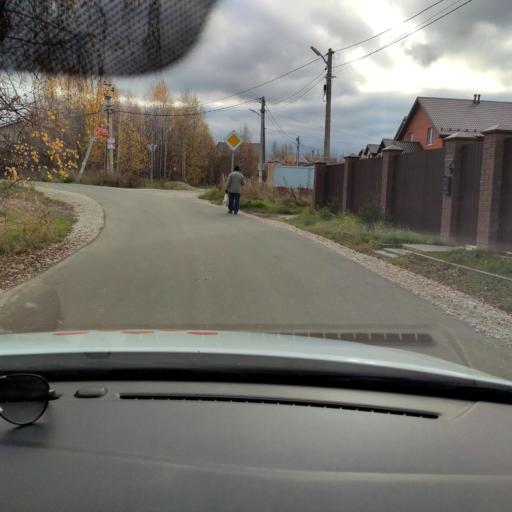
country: RU
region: Tatarstan
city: Stolbishchi
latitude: 55.7362
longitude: 49.2681
